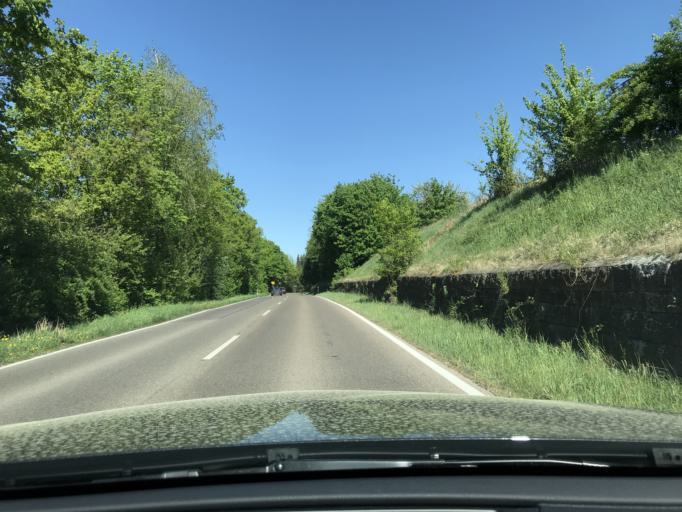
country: DE
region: Baden-Wuerttemberg
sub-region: Regierungsbezirk Stuttgart
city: Weinstadt-Endersbach
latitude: 48.8249
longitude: 9.3766
